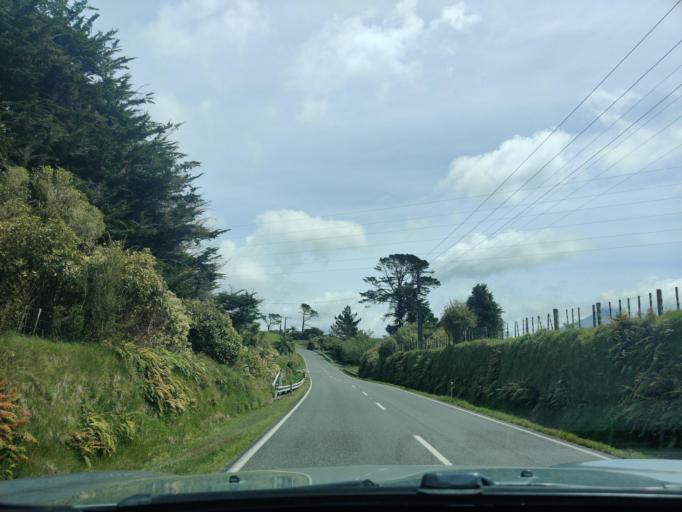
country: NZ
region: Taranaki
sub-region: South Taranaki District
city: Eltham
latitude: -39.3754
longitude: 174.1851
